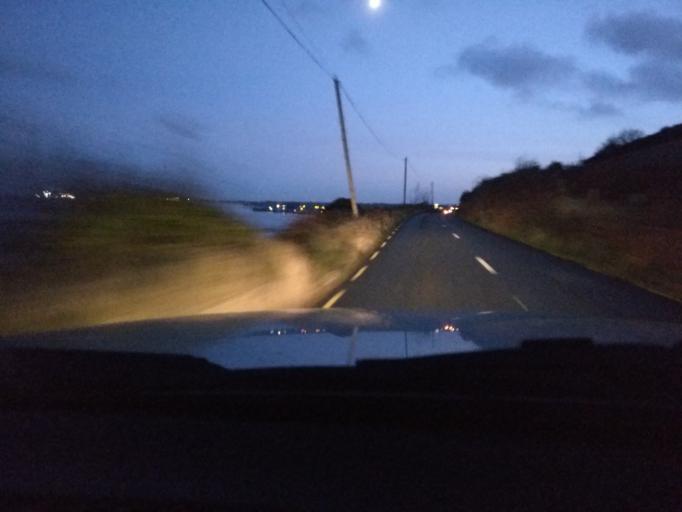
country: IE
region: Leinster
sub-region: Lu
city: Carlingford
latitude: 54.0511
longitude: -6.1936
